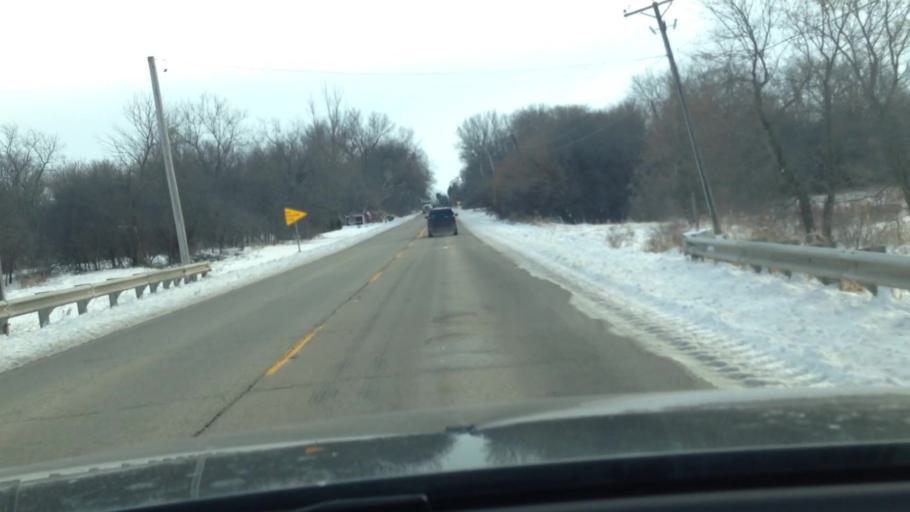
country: US
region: Illinois
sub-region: McHenry County
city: Hebron
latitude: 42.4862
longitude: -88.4425
